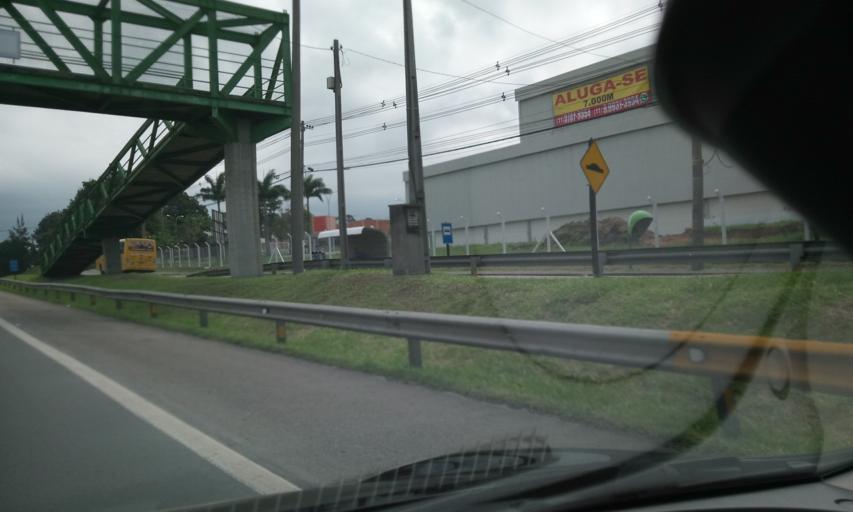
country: BR
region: Sao Paulo
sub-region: Jundiai
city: Jundiai
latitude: -23.1790
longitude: -46.9589
